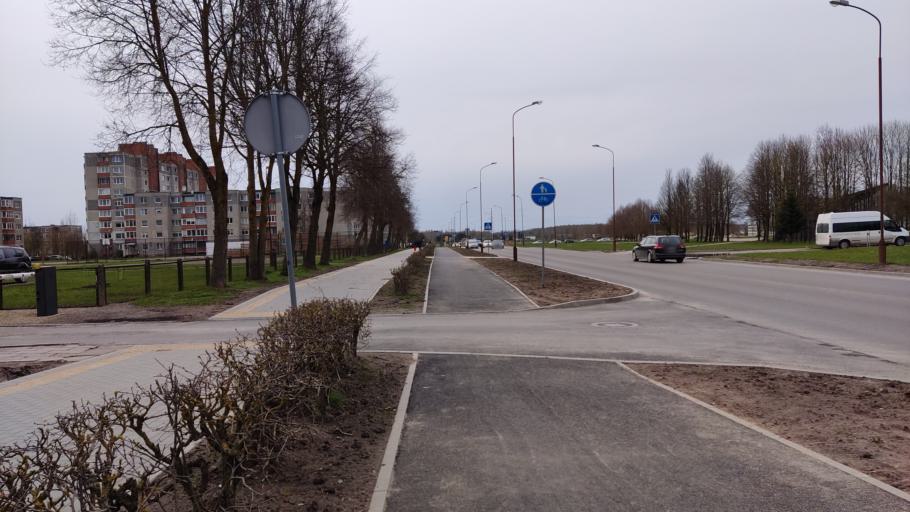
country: LT
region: Siauliu apskritis
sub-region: Siauliai
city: Siauliai
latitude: 55.9176
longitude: 23.2647
